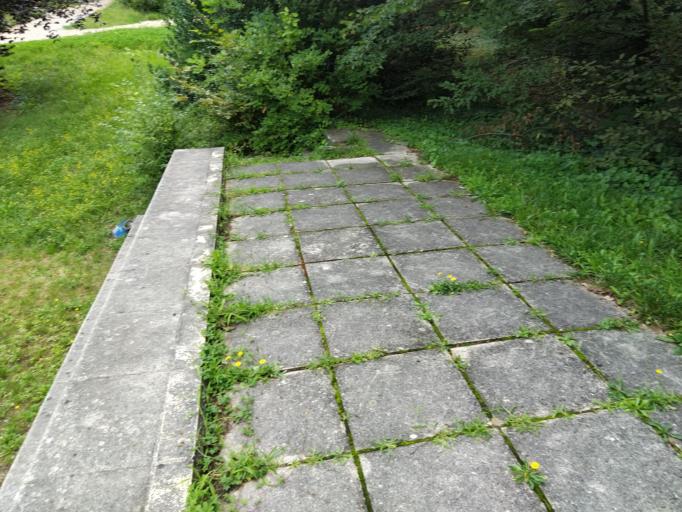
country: FR
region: Rhone-Alpes
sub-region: Departement de l'Ardeche
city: Annonay
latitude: 45.2459
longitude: 4.6695
